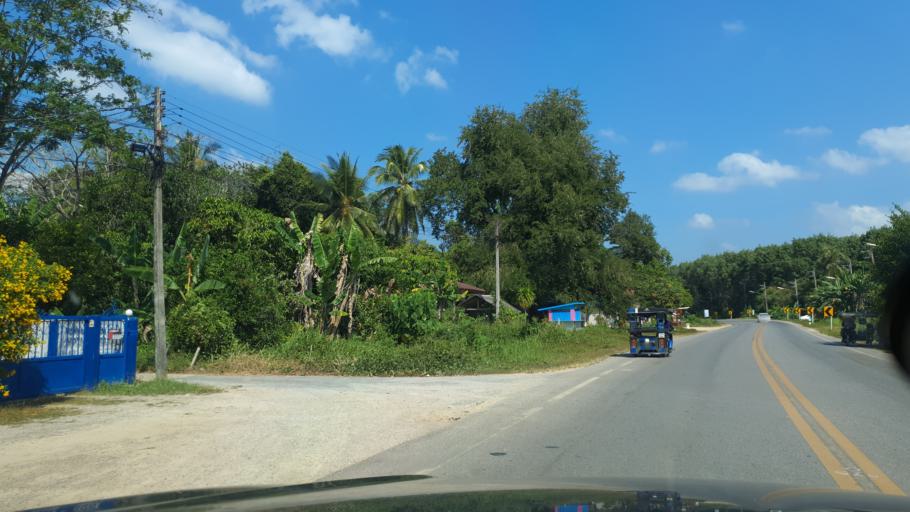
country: TH
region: Phangnga
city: Ban Ao Nang
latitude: 8.0626
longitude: 98.8593
